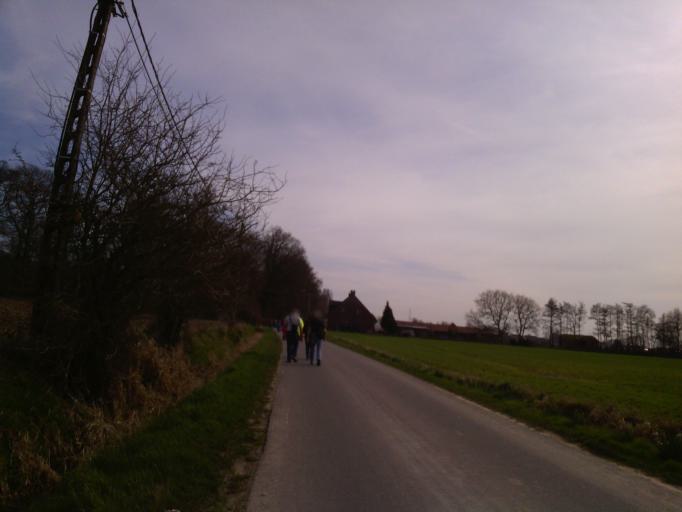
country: BE
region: Flanders
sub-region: Provincie West-Vlaanderen
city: Ieper
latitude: 50.8612
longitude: 2.8139
